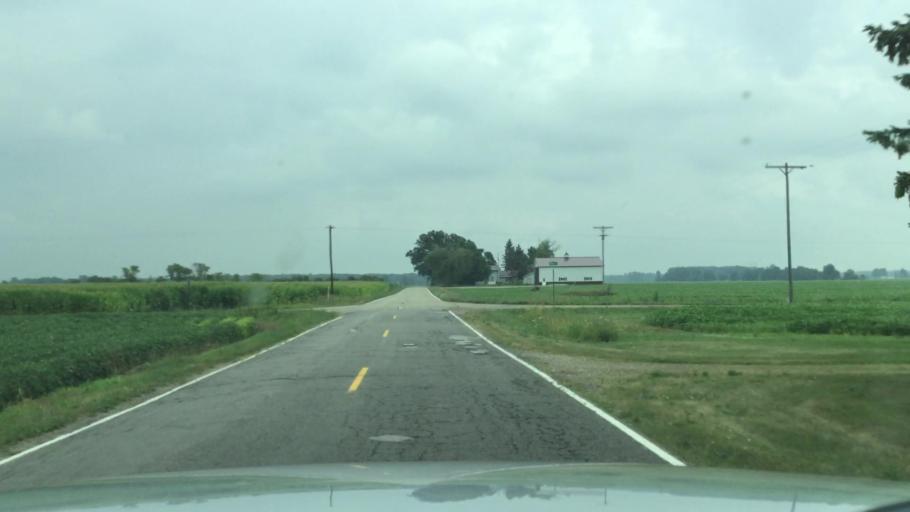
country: US
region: Michigan
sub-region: Shiawassee County
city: New Haven
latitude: 43.0722
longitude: -84.2261
